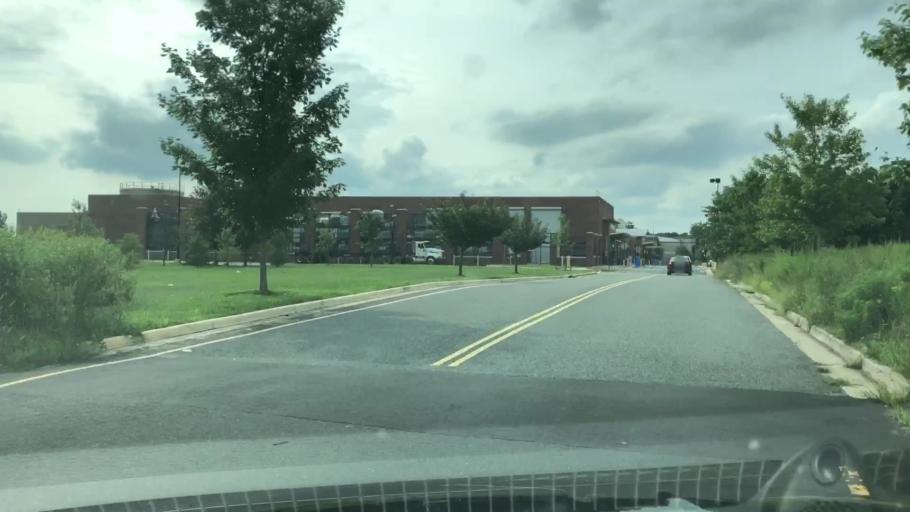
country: US
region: Virginia
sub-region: Stafford County
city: Falmouth
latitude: 38.3690
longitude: -77.5268
